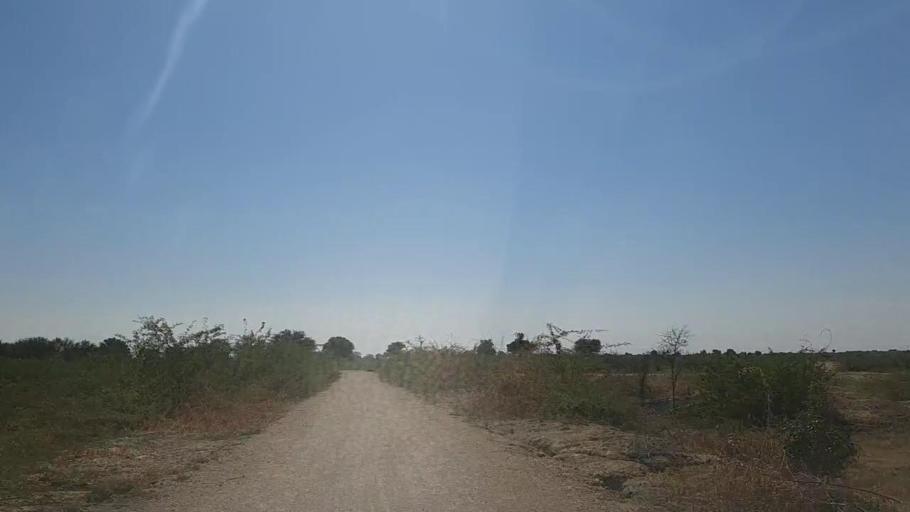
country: PK
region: Sindh
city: Dhoro Naro
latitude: 25.3536
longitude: 69.5338
